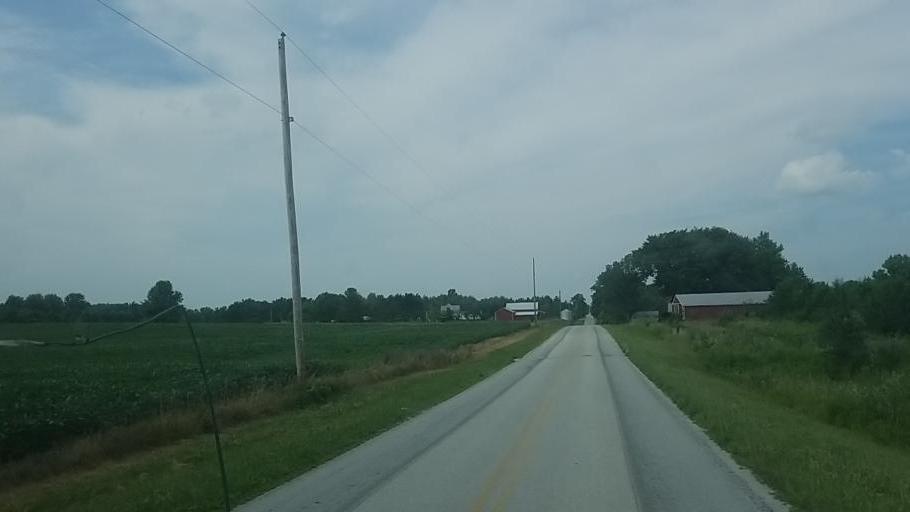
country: US
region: Ohio
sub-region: Hardin County
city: Forest
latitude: 40.7777
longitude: -83.5764
